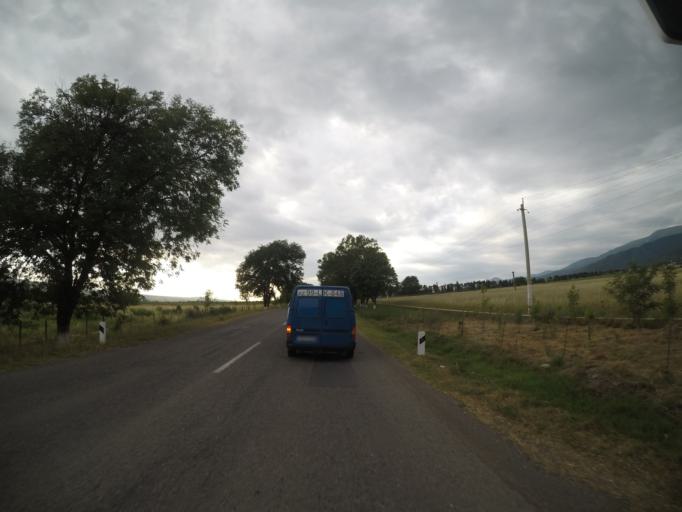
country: AZ
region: Ismayilli
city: Ismayilli
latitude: 40.7751
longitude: 48.1980
